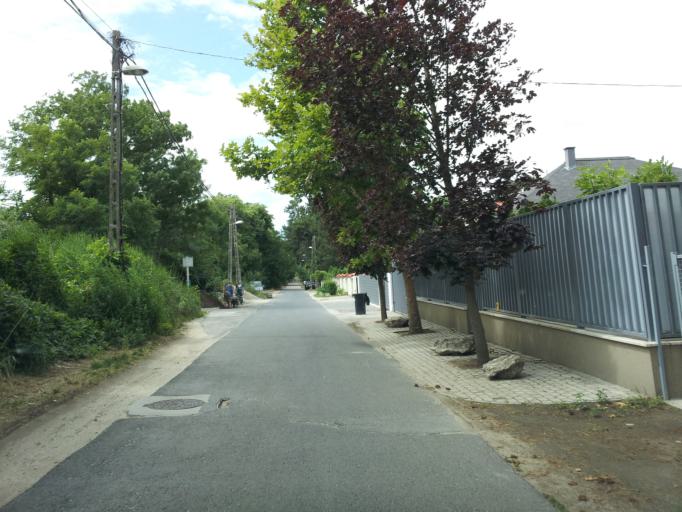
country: HU
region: Somogy
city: Balatonszabadi
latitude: 46.9439
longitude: 18.1355
